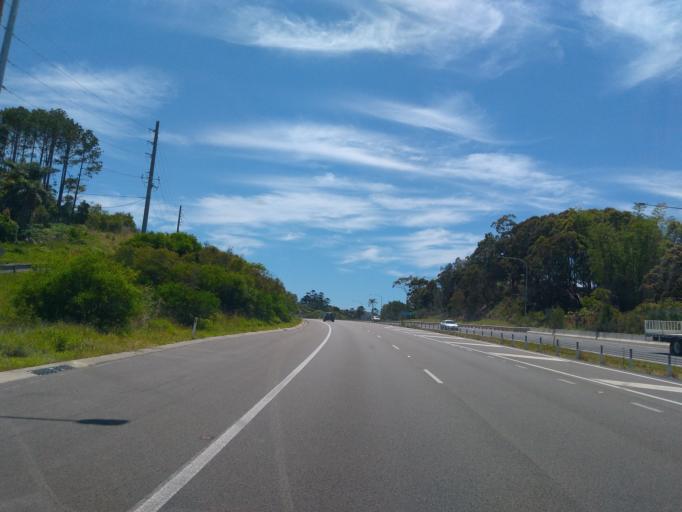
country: AU
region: New South Wales
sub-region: Coffs Harbour
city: Moonee Beach
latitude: -30.2475
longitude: 153.1393
